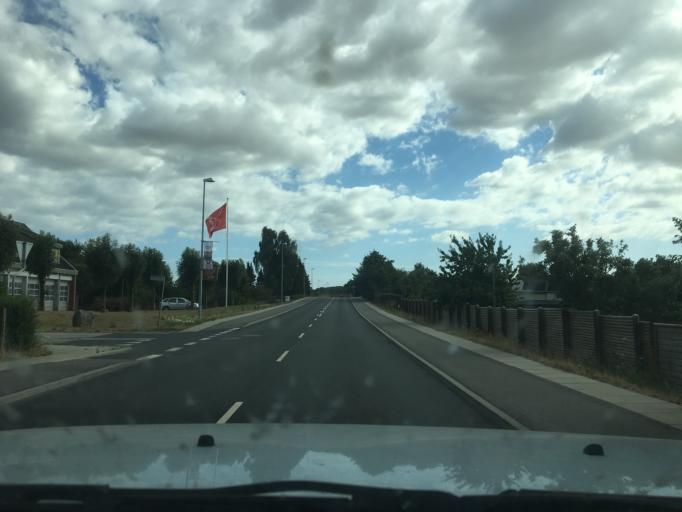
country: DK
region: Central Jutland
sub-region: Syddjurs Kommune
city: Hornslet
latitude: 56.3099
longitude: 10.3184
